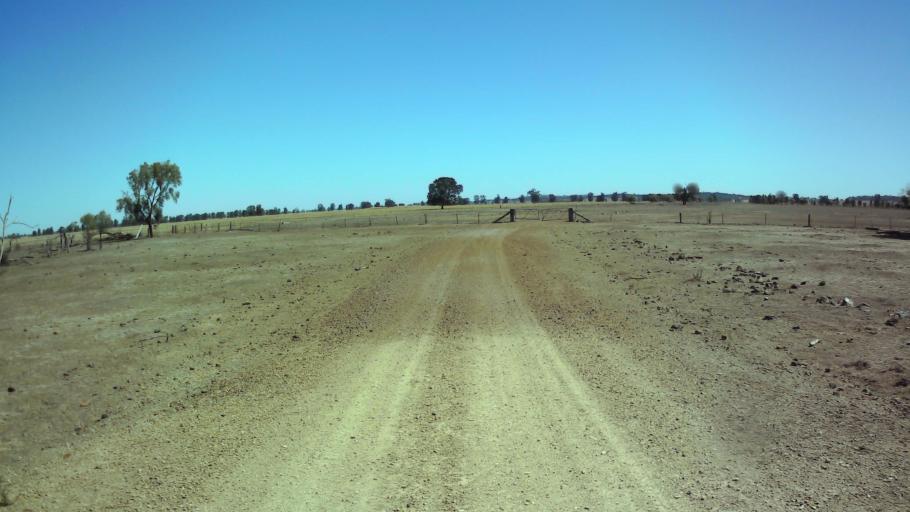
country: AU
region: New South Wales
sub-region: Forbes
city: Forbes
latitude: -33.7252
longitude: 147.6656
